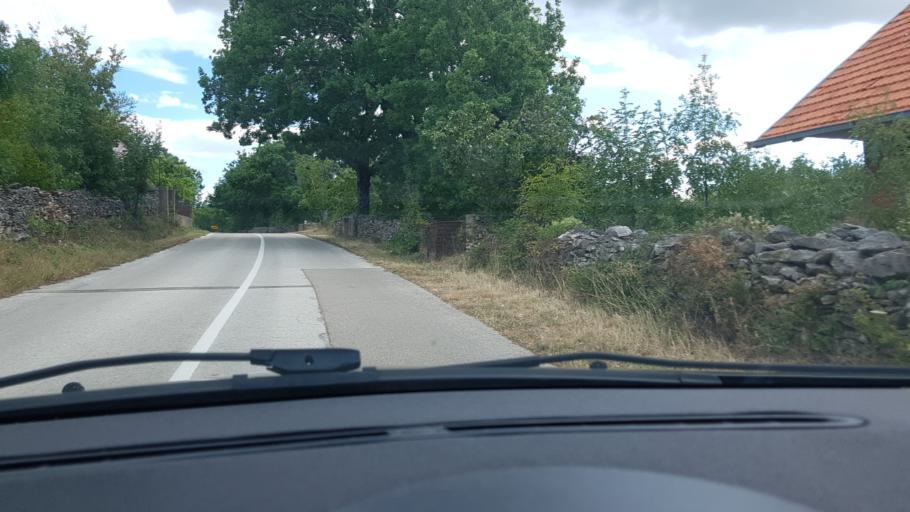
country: HR
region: Sibensko-Kniniska
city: Kistanje
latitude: 44.0769
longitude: 15.9326
